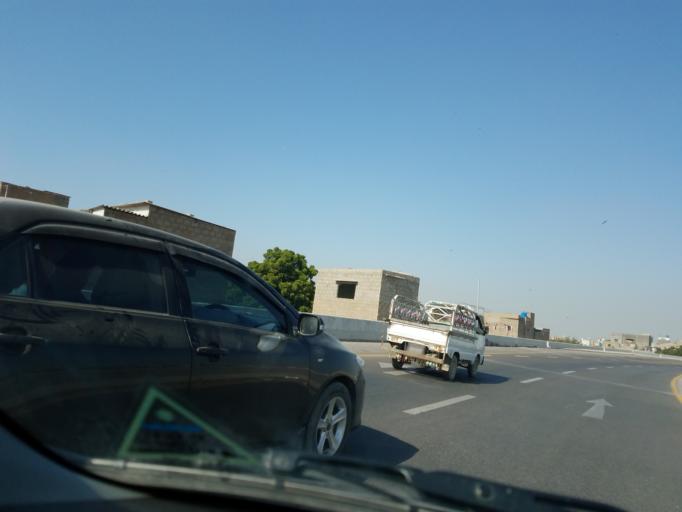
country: PK
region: Sindh
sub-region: Karachi District
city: Karachi
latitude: 24.8823
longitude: 67.0182
